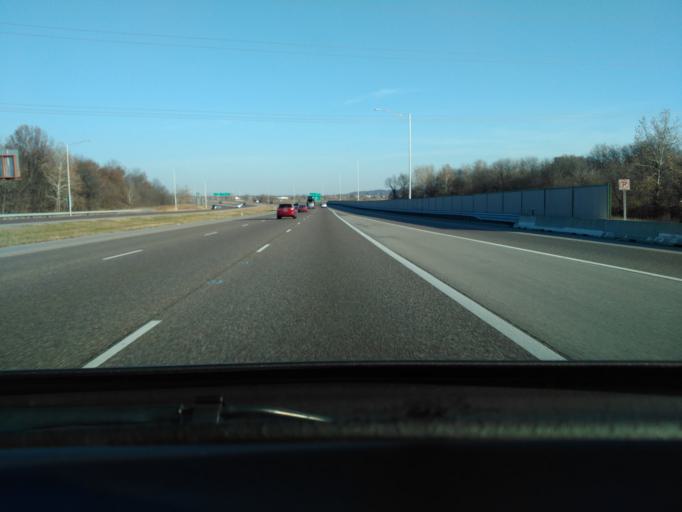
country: US
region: Illinois
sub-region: Saint Clair County
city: Caseyville
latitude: 38.6623
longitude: -90.0300
